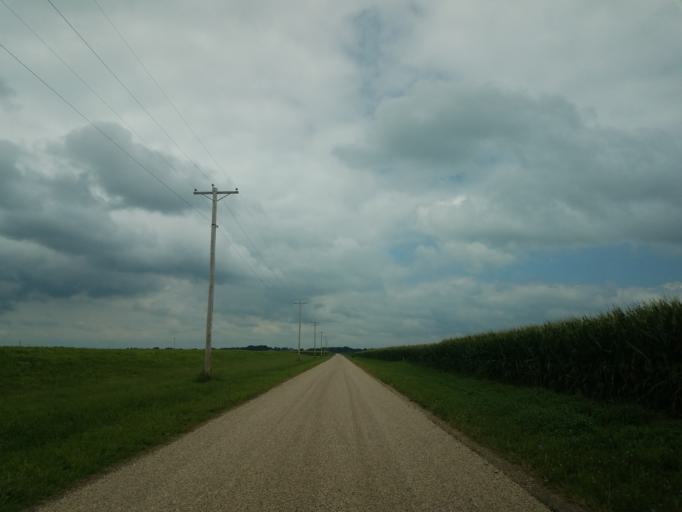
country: US
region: Illinois
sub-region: McLean County
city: Twin Grove
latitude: 40.4369
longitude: -89.0583
